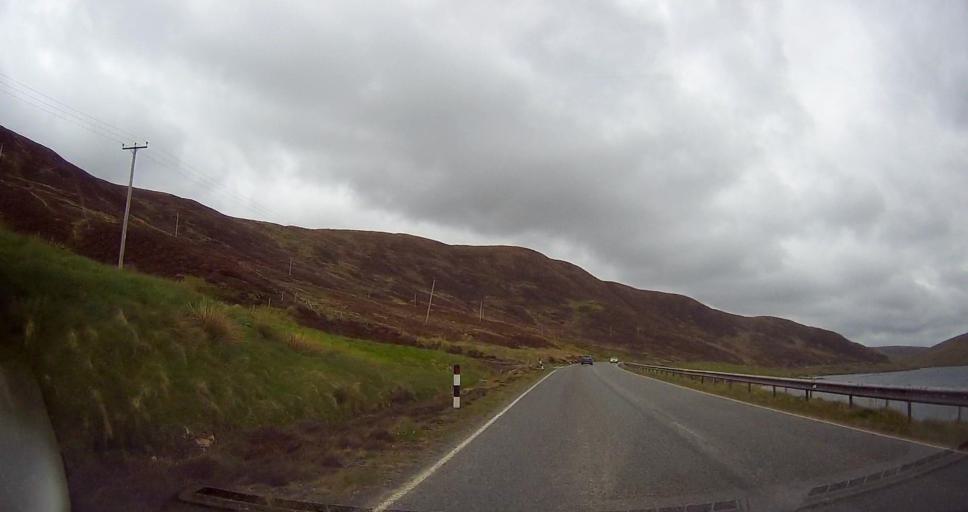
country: GB
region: Scotland
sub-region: Shetland Islands
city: Lerwick
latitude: 60.3693
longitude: -1.2984
